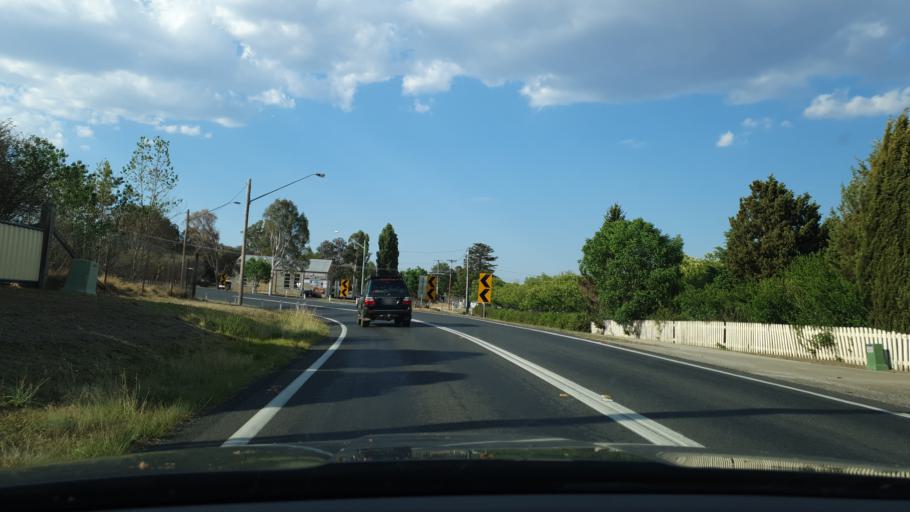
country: AU
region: New South Wales
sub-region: Tenterfield Municipality
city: Carrolls Creek
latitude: -29.0420
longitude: 152.0213
